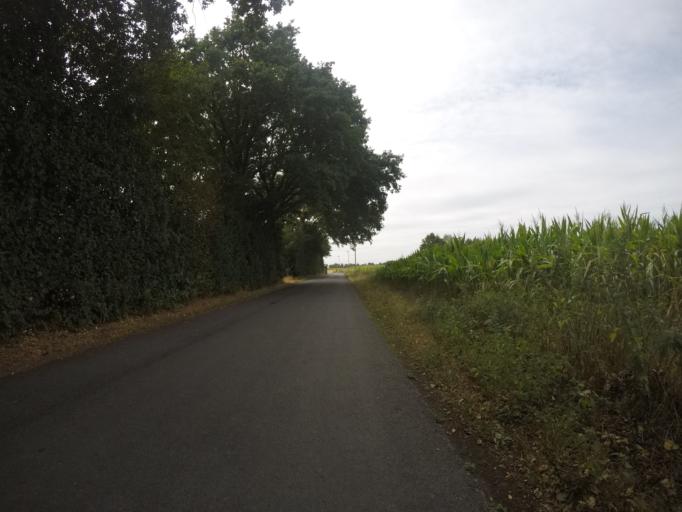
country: DE
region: North Rhine-Westphalia
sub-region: Regierungsbezirk Dusseldorf
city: Bocholt
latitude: 51.8539
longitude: 6.5833
